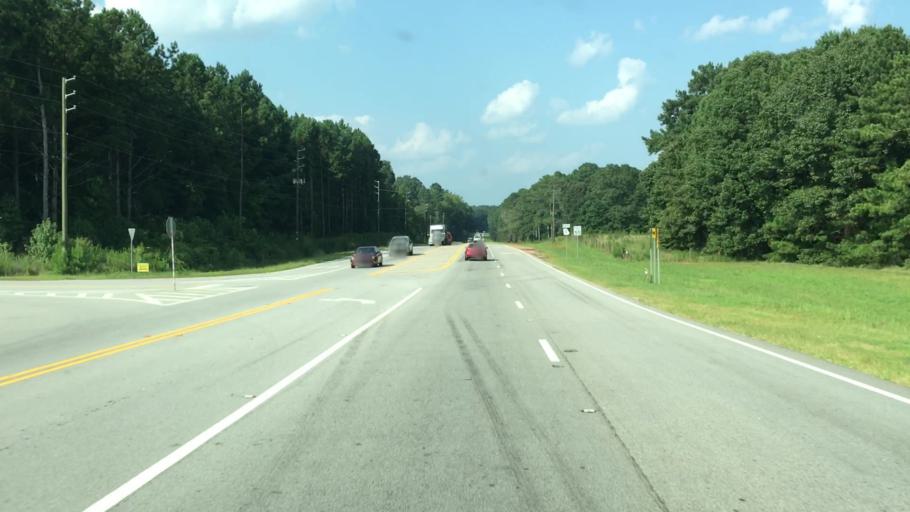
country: US
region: Georgia
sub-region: Walton County
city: Social Circle
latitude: 33.6151
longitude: -83.7488
